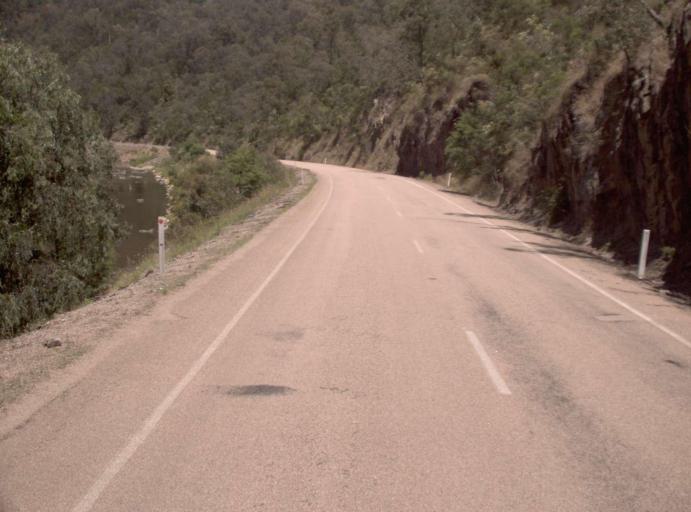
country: AU
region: Victoria
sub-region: East Gippsland
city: Bairnsdale
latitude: -37.4671
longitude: 147.8296
